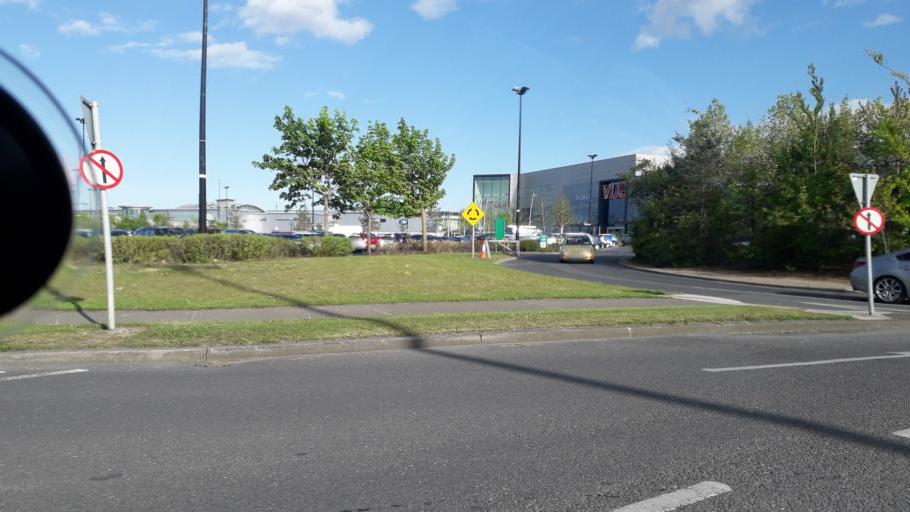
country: IE
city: Palmerstown
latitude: 53.3536
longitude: -6.3956
